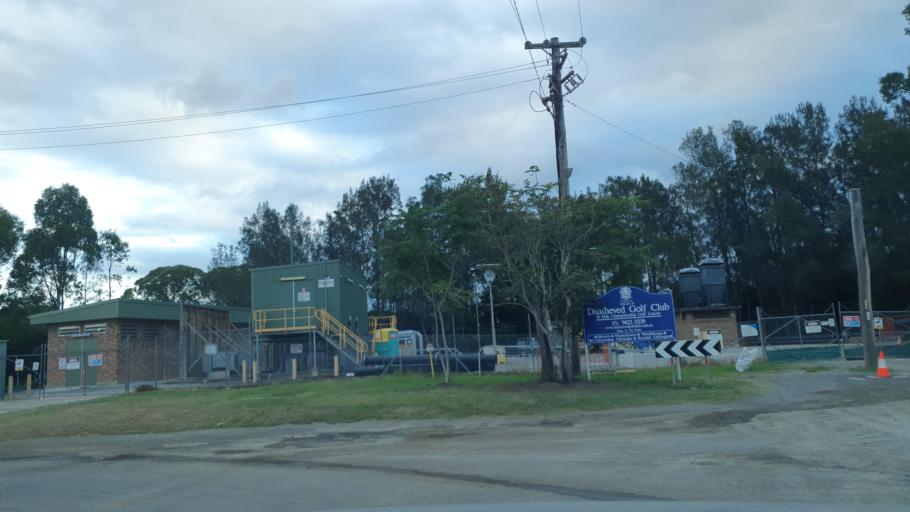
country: AU
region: New South Wales
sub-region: Penrith Municipality
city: Werrington County
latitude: -33.7403
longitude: 150.7620
